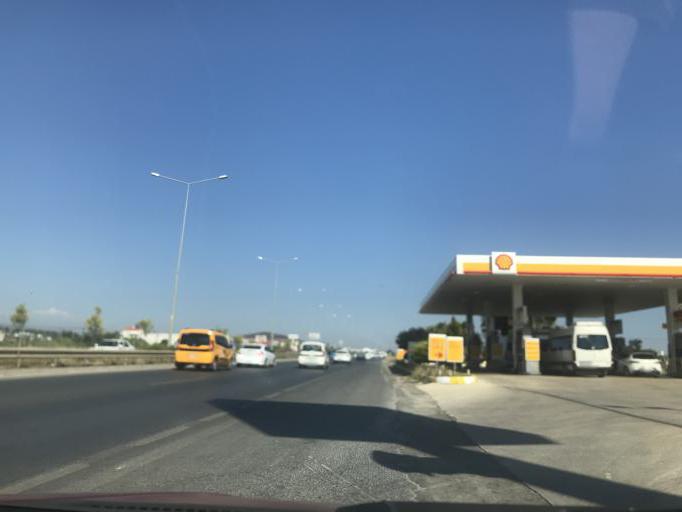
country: TR
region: Antalya
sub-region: Manavgat
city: Side
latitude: 36.8116
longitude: 31.3749
